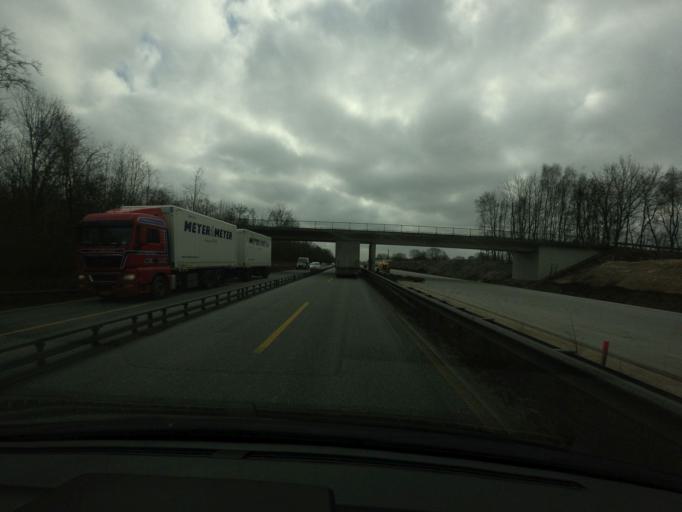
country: DE
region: Schleswig-Holstein
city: Alveslohe
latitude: 53.7994
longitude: 9.9313
